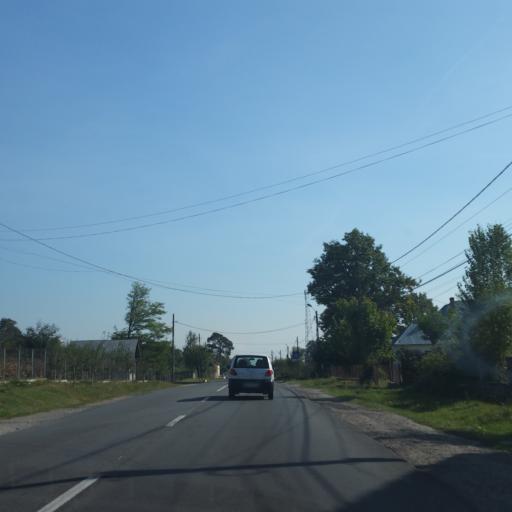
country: RO
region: Arges
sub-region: Comuna Baiculesti
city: Baiculesti
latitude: 45.0930
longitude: 24.6738
